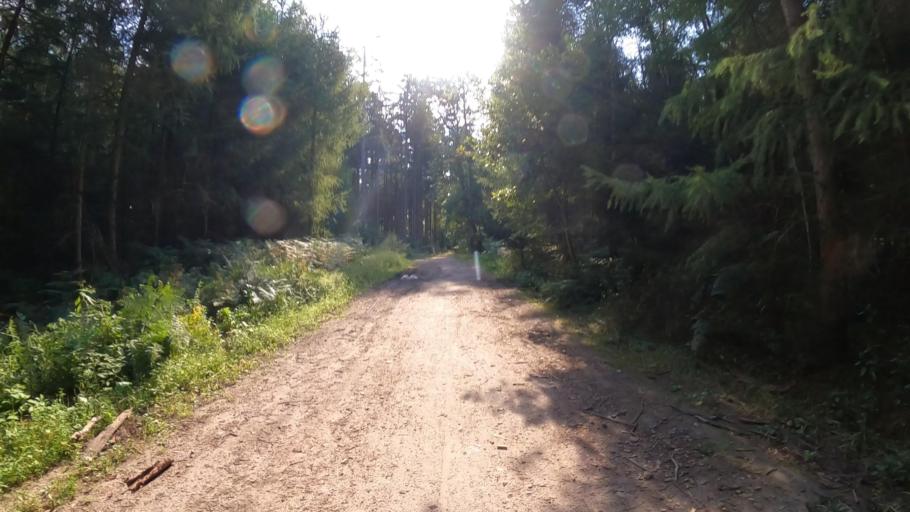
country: DE
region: Schleswig-Holstein
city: Kroppelshagen-Fahrendorf
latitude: 53.4961
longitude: 10.3397
